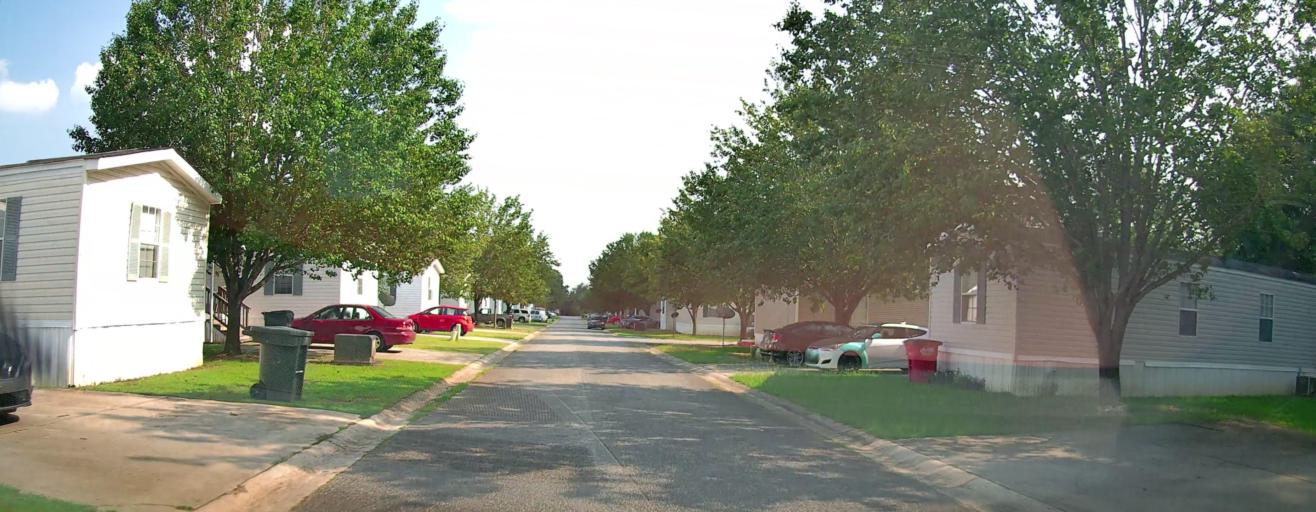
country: US
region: Georgia
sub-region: Houston County
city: Centerville
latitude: 32.6458
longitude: -83.6892
